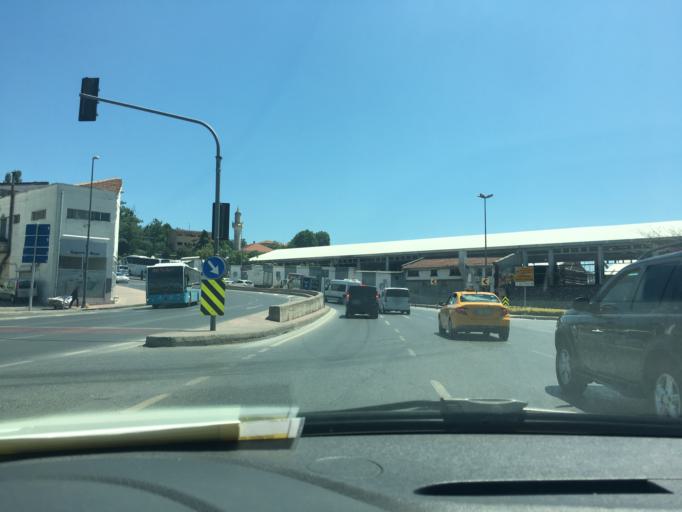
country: TR
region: Istanbul
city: Eminoenue
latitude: 41.0301
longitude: 28.9678
